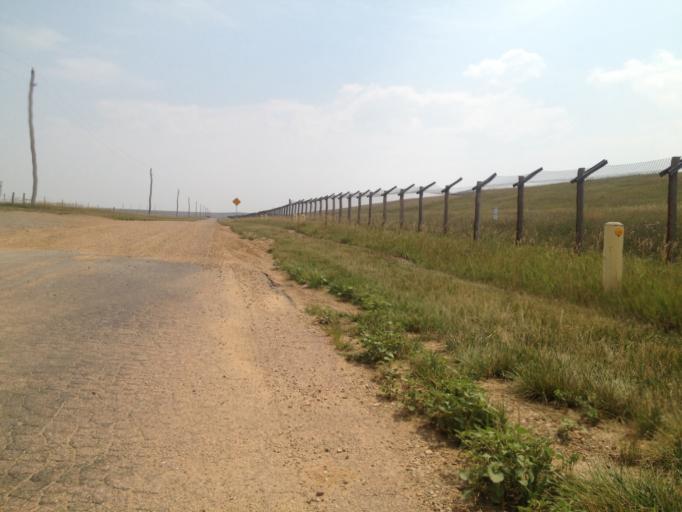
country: US
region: Colorado
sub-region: Boulder County
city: Superior
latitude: 39.9493
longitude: -105.1989
